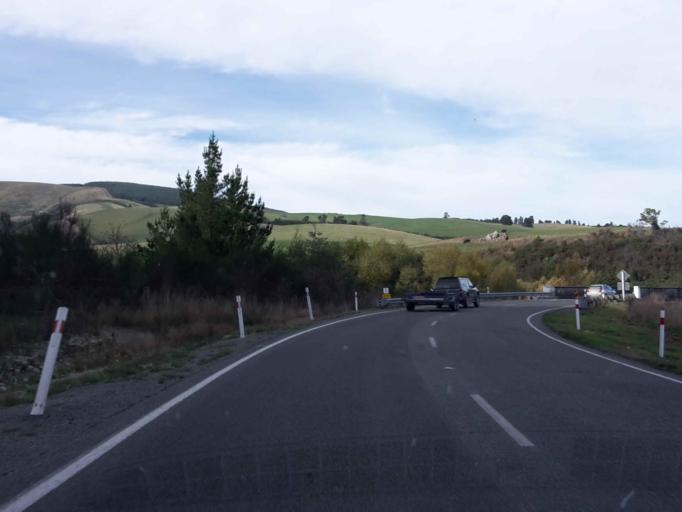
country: NZ
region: Canterbury
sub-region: Timaru District
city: Pleasant Point
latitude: -44.0802
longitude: 170.9777
